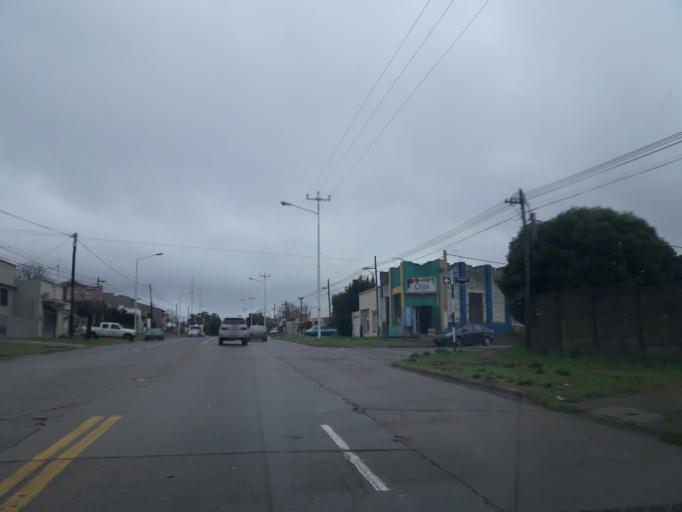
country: AR
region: Buenos Aires
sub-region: Partido de Tandil
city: Tandil
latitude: -37.3197
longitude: -59.1615
